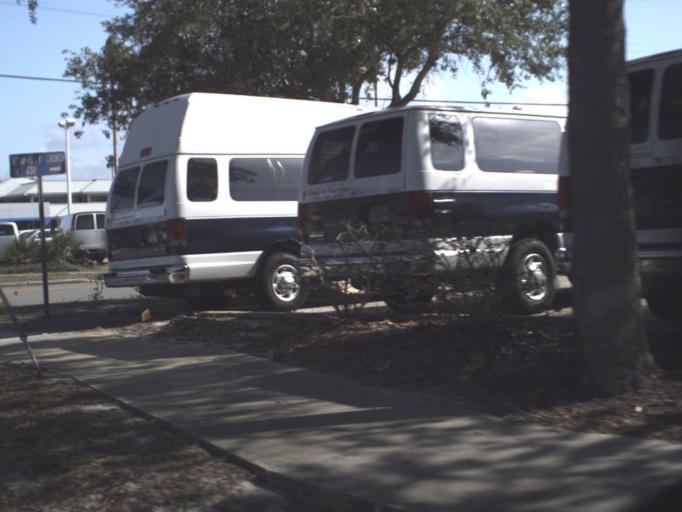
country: US
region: Florida
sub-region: Brevard County
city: Melbourne
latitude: 28.1001
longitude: -80.6132
